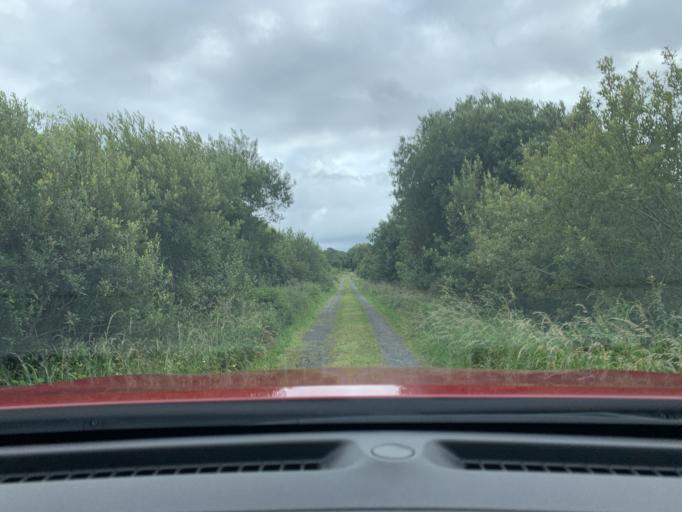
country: IE
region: Connaught
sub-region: County Leitrim
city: Kinlough
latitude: 54.4586
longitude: -8.3564
